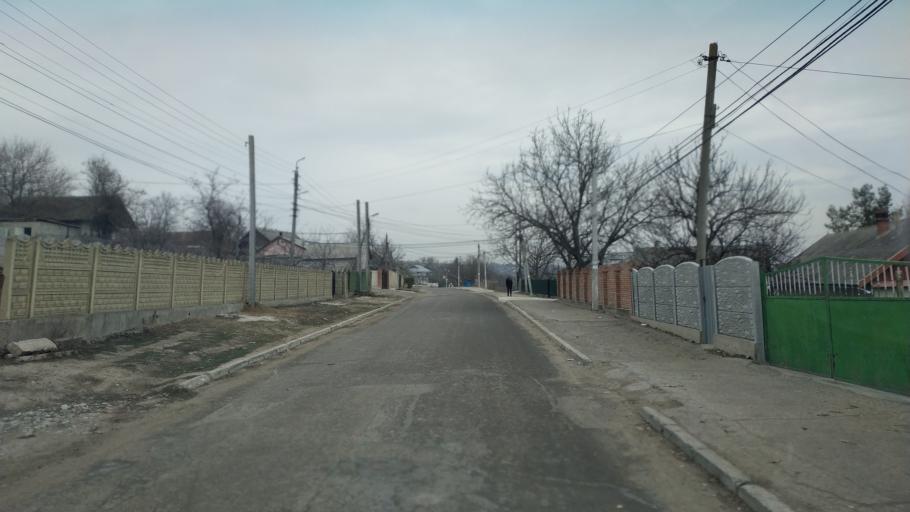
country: MD
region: Chisinau
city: Singera
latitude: 46.9331
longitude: 28.9891
